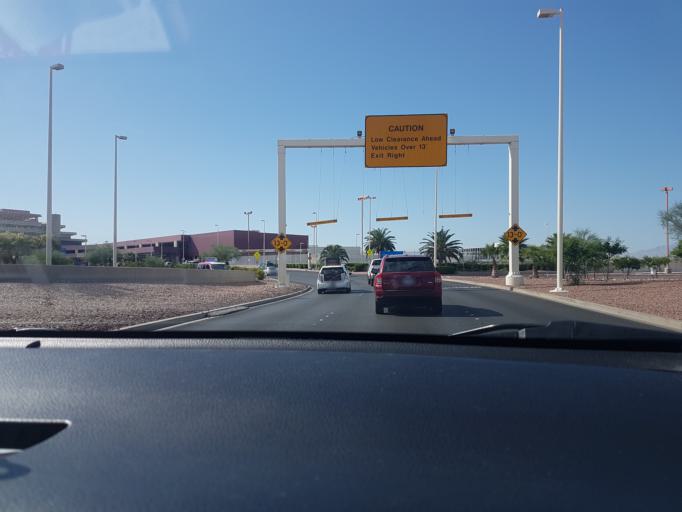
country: US
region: Nevada
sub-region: Clark County
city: Paradise
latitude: 36.0886
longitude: -115.1505
